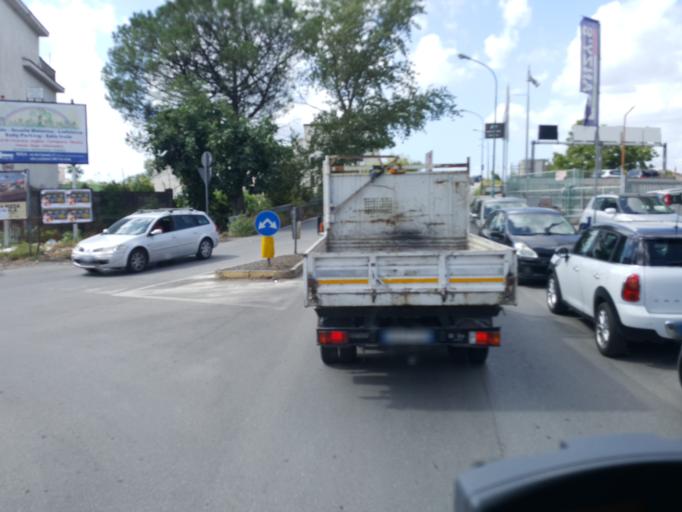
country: IT
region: Campania
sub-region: Provincia di Napoli
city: Nola
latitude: 40.9186
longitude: 14.5340
